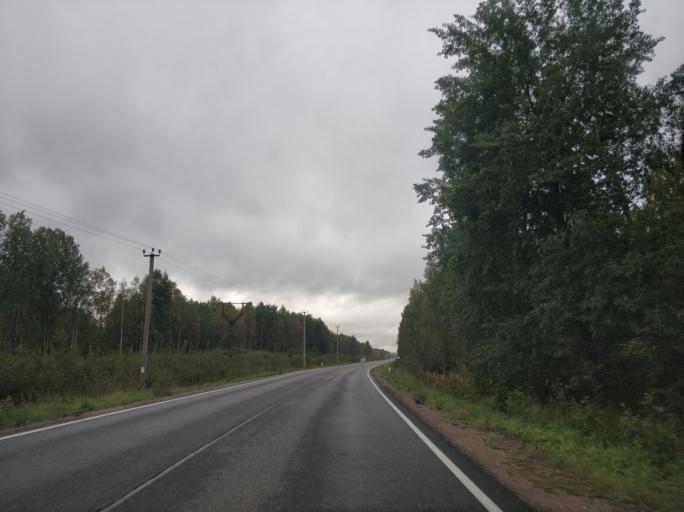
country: RU
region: Leningrad
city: Borisova Griva
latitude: 60.1145
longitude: 30.9635
